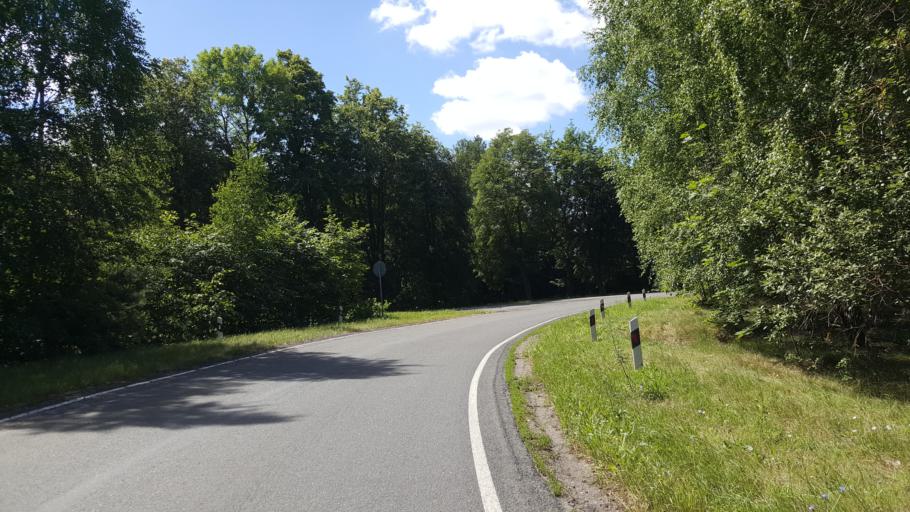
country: BY
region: Brest
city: Kamyanyets
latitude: 52.3434
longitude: 23.9110
